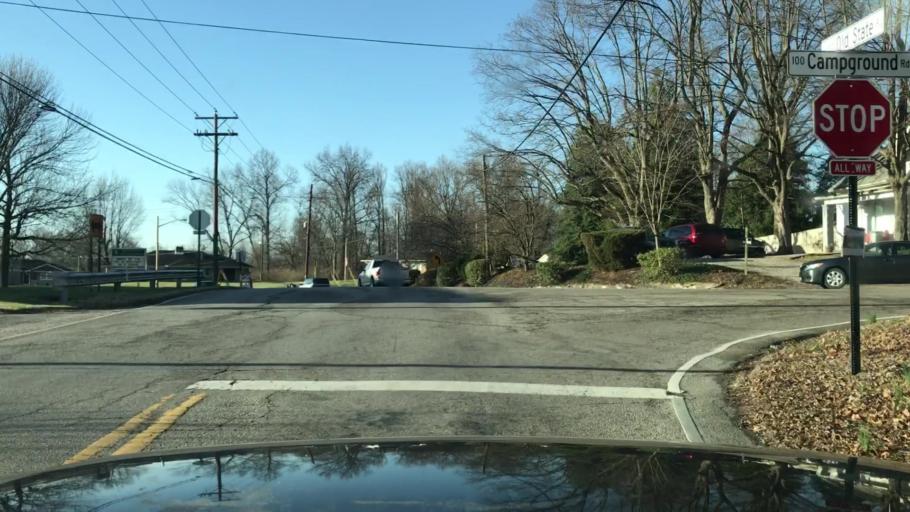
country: US
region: Indiana
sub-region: Vanderburgh County
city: Highland
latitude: 38.0359
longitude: -87.5642
